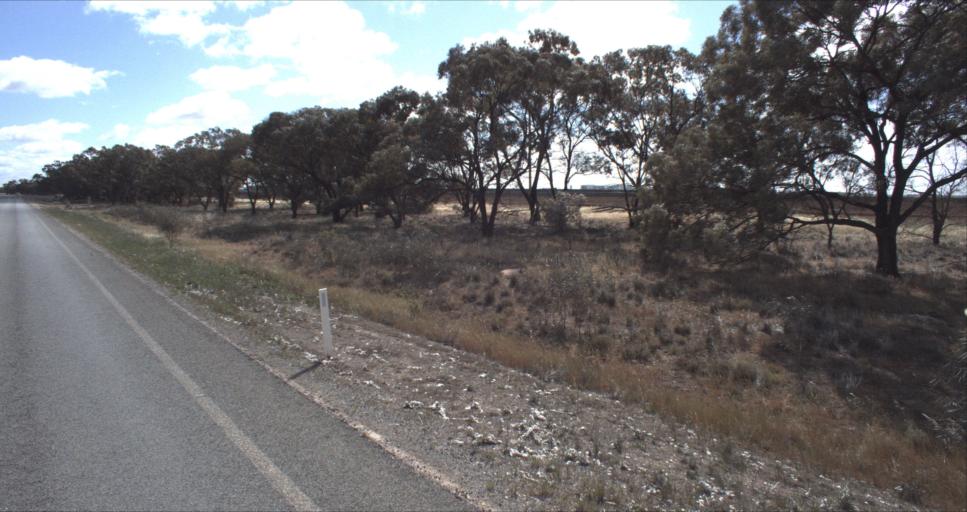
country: AU
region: New South Wales
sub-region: Murrumbidgee Shire
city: Darlington Point
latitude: -34.5780
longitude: 146.1657
